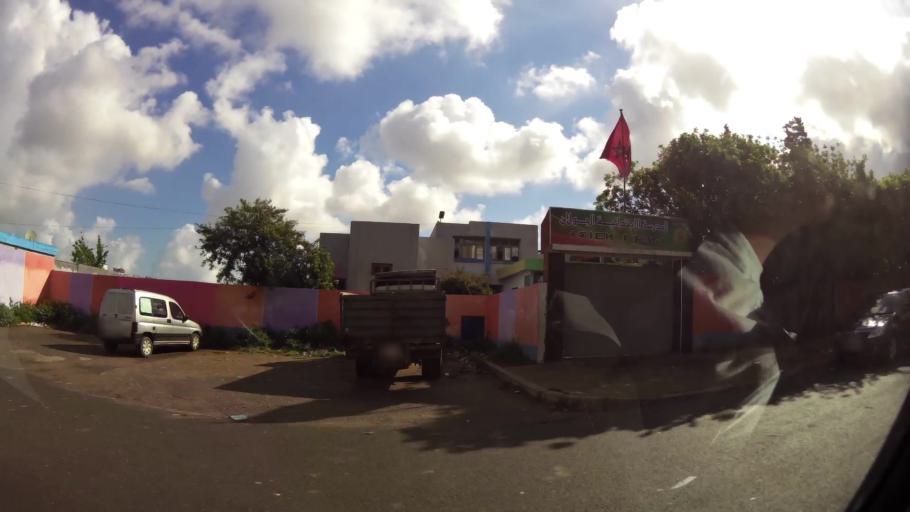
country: MA
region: Grand Casablanca
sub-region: Mediouna
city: Tit Mellil
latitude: 33.5754
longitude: -7.5297
